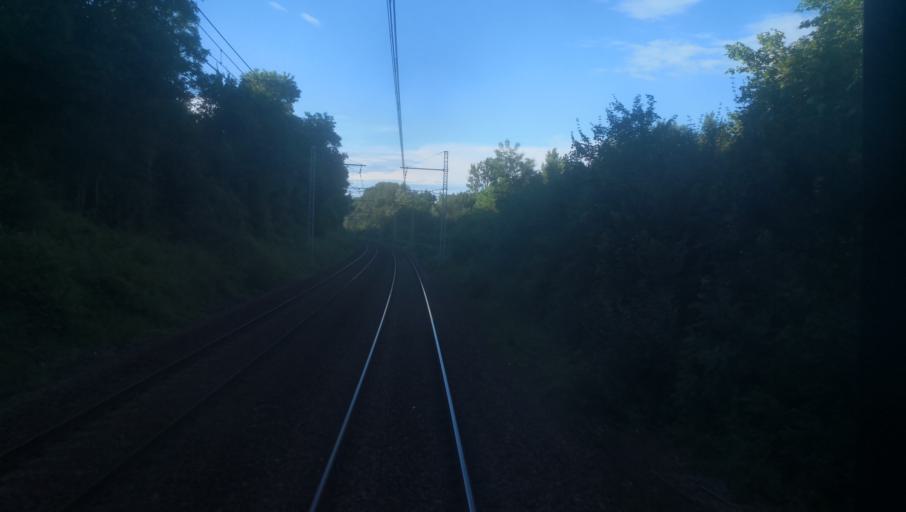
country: FR
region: Centre
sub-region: Departement de l'Indre
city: Reuilly
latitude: 47.1071
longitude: 2.0489
